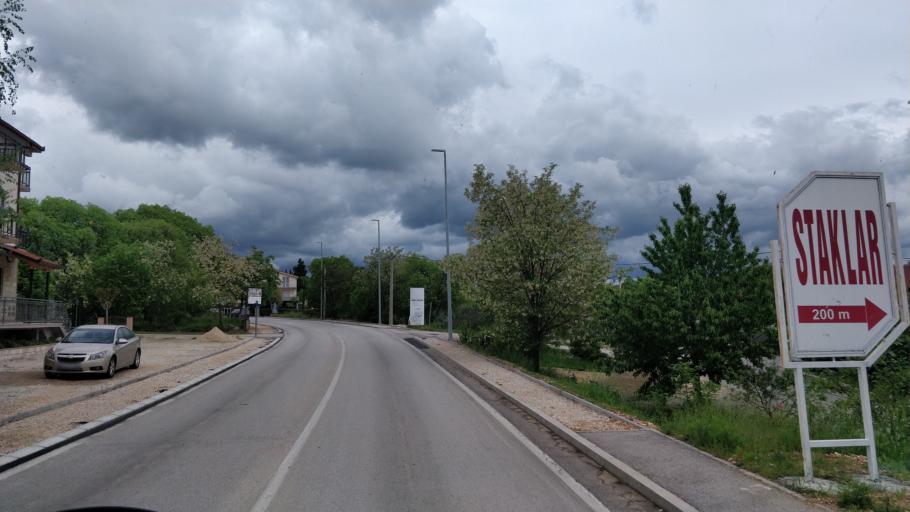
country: BA
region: Federation of Bosnia and Herzegovina
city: Ljubuski
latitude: 43.1889
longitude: 17.5373
